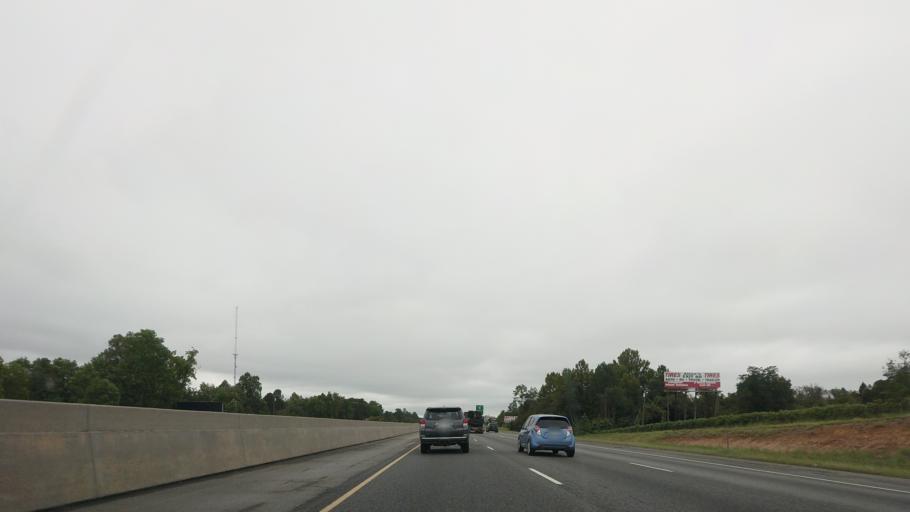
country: US
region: Georgia
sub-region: Turner County
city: Ashburn
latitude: 31.7447
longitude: -83.6586
